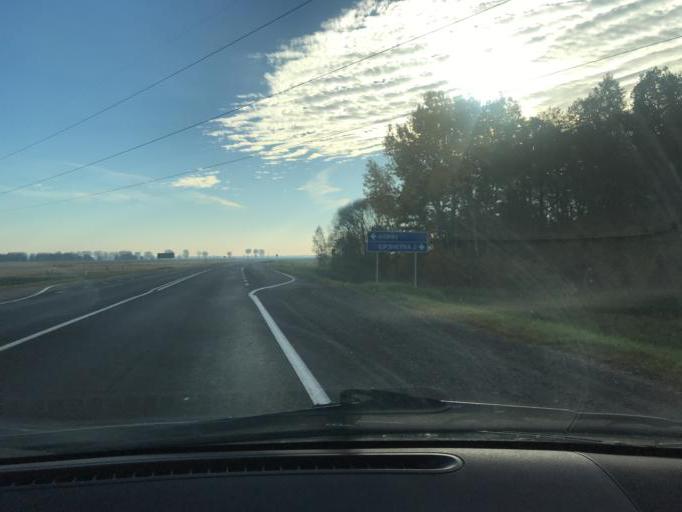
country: BY
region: Brest
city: Drahichyn
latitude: 52.2240
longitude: 25.1543
